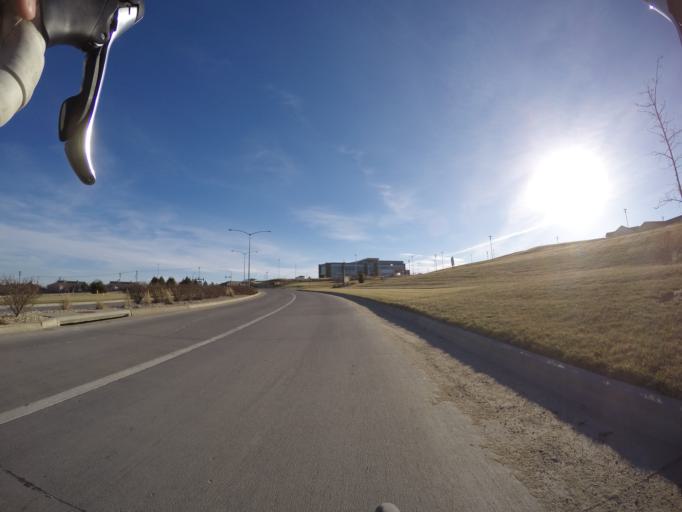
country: US
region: Kansas
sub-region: Riley County
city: Manhattan
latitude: 39.2049
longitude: -96.6356
